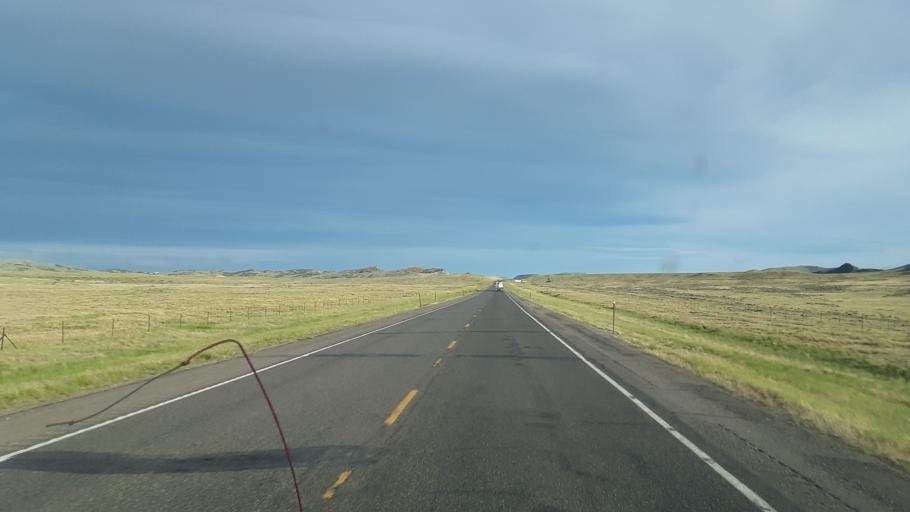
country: US
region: Wyoming
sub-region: Park County
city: Cody
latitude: 44.4725
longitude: -109.0193
